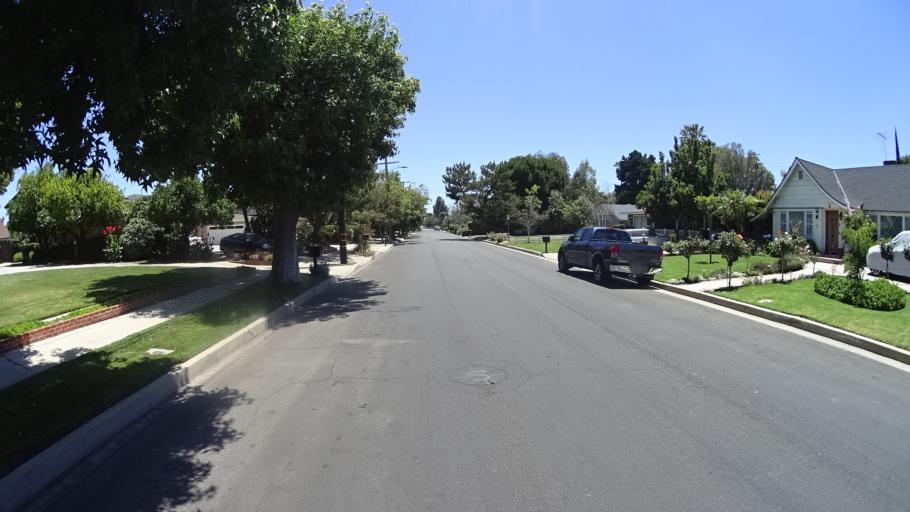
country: US
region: California
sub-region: Los Angeles County
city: Van Nuys
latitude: 34.1965
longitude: -118.4705
